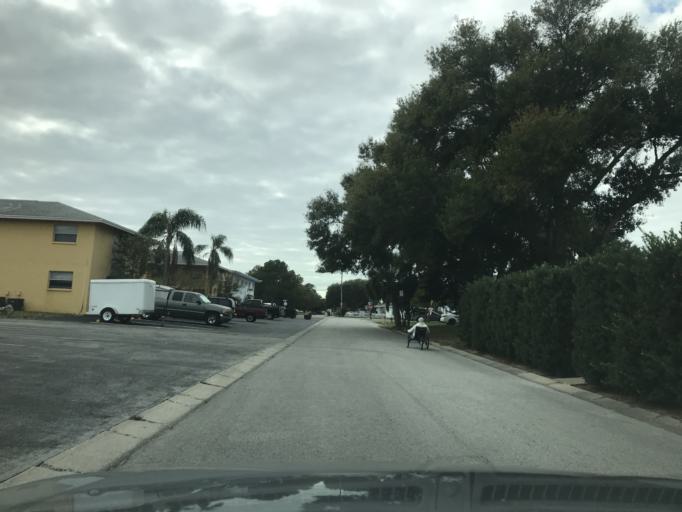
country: US
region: Florida
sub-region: Pinellas County
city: Belleair
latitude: 27.9325
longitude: -82.7859
